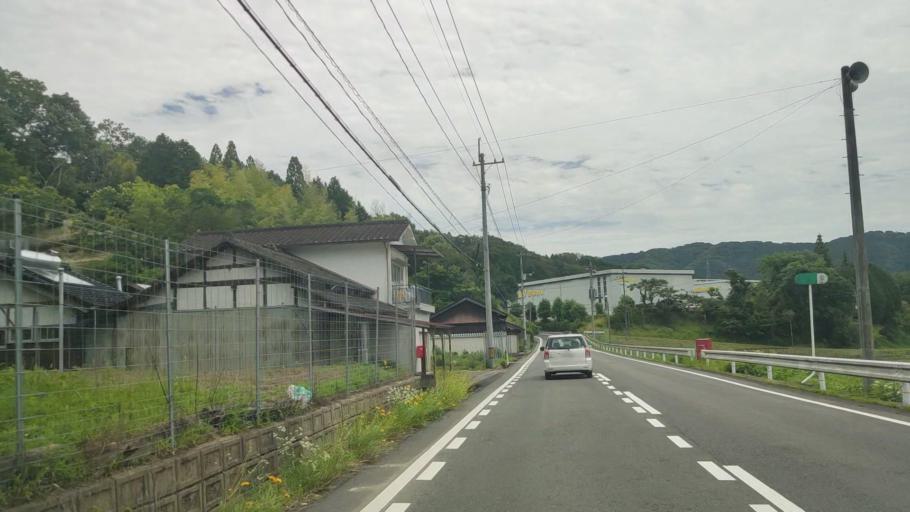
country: JP
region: Hyogo
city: Yamazakicho-nakabirose
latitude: 35.1010
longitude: 134.3150
